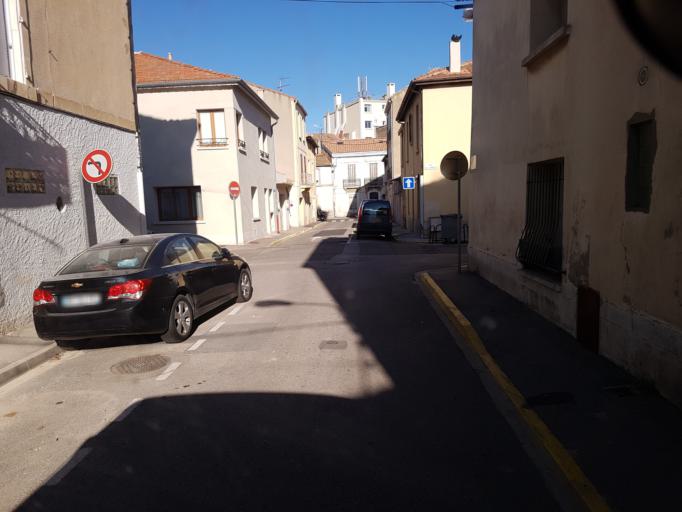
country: FR
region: Languedoc-Roussillon
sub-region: Departement de l'Aude
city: Narbonne
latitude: 43.1801
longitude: 3.0060
